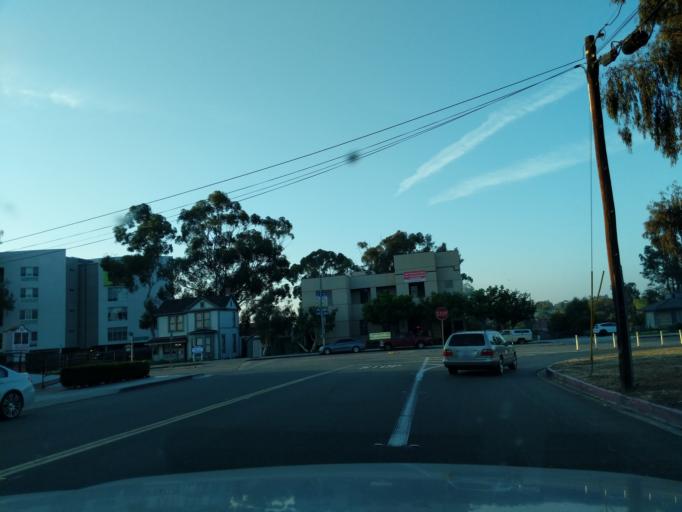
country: US
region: California
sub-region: San Diego County
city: San Diego
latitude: 32.7498
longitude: -117.1563
